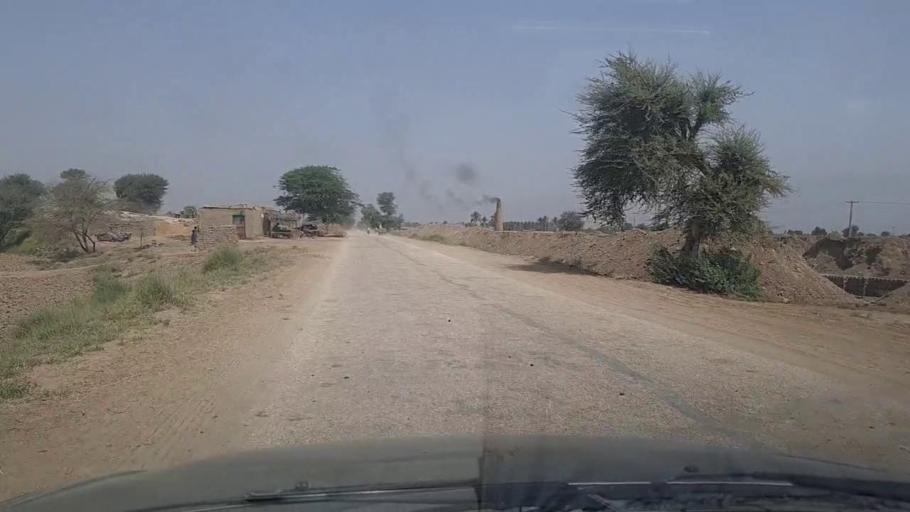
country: PK
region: Sindh
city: Setharja Old
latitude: 27.1471
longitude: 68.5248
